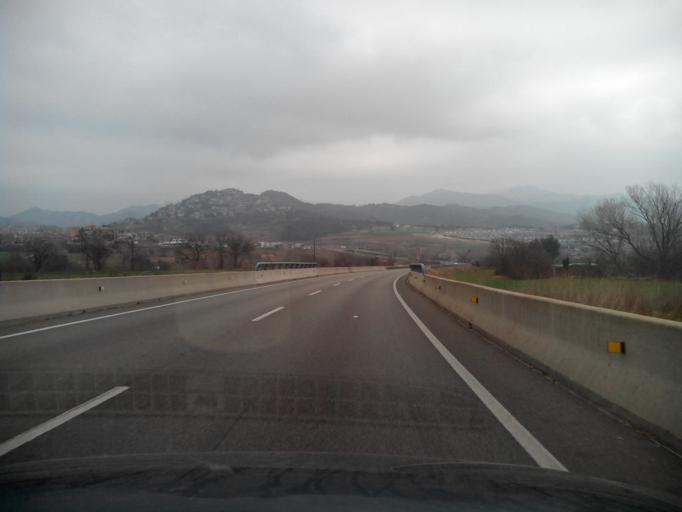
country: ES
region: Catalonia
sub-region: Provincia de Barcelona
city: Berga
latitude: 42.0919
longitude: 1.8384
